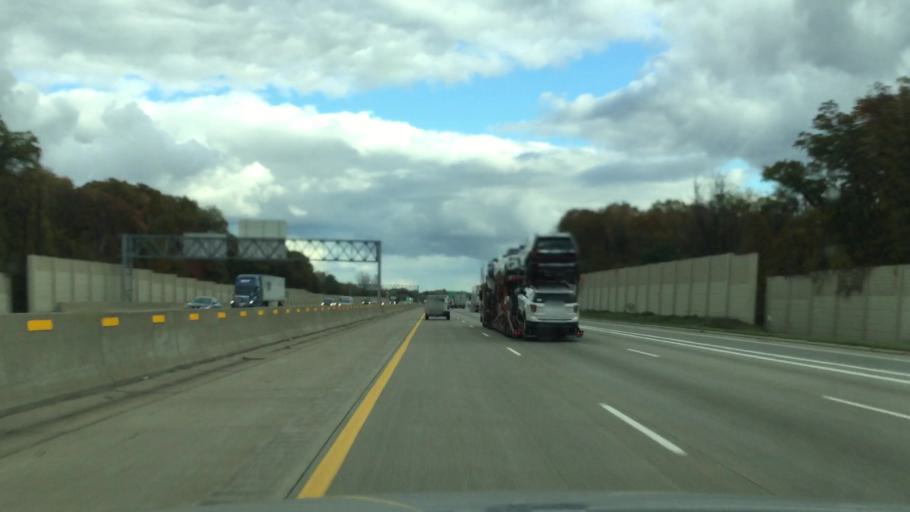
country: US
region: Michigan
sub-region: Kalamazoo County
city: Portage
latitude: 42.2378
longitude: -85.6099
